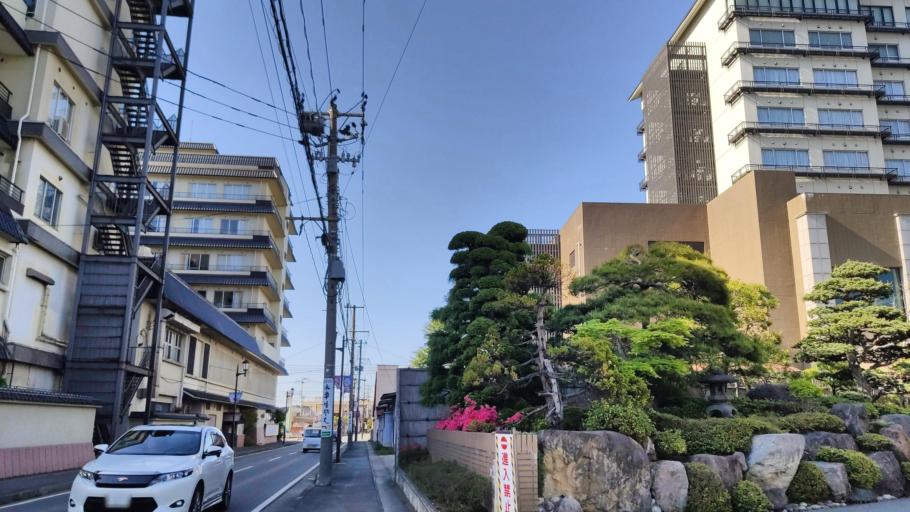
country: JP
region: Yamagata
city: Tendo
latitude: 38.3588
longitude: 140.3818
